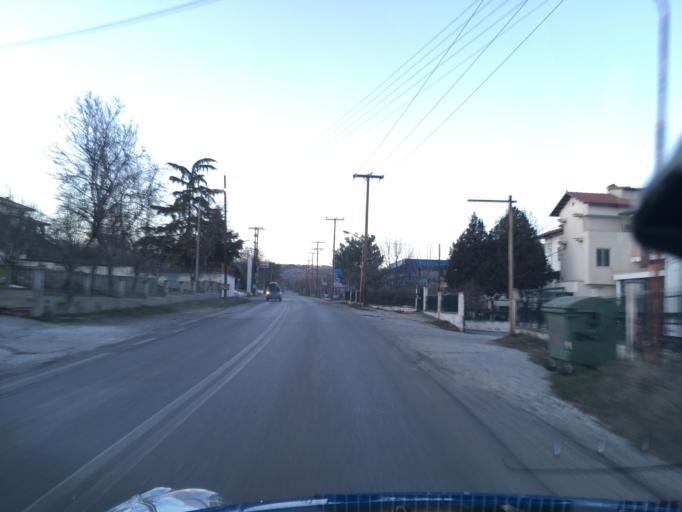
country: GR
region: West Macedonia
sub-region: Nomos Kozanis
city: Kozani
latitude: 40.2808
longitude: 21.7831
